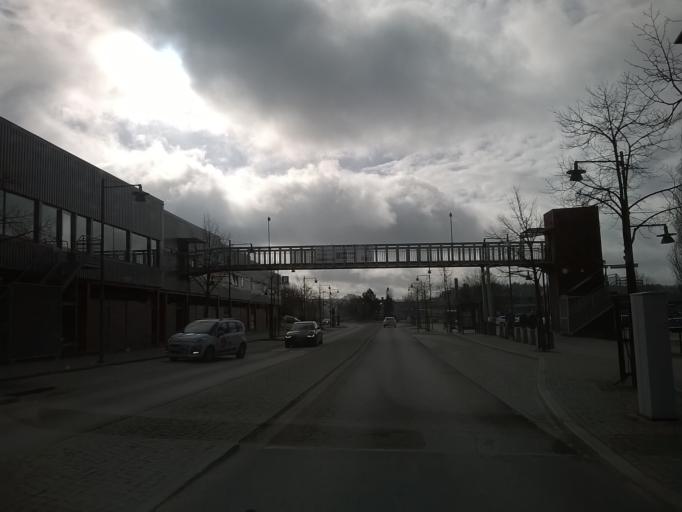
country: SE
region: Vaestra Goetaland
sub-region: Kungalvs Kommun
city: Kungalv
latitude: 57.8695
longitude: 11.9820
